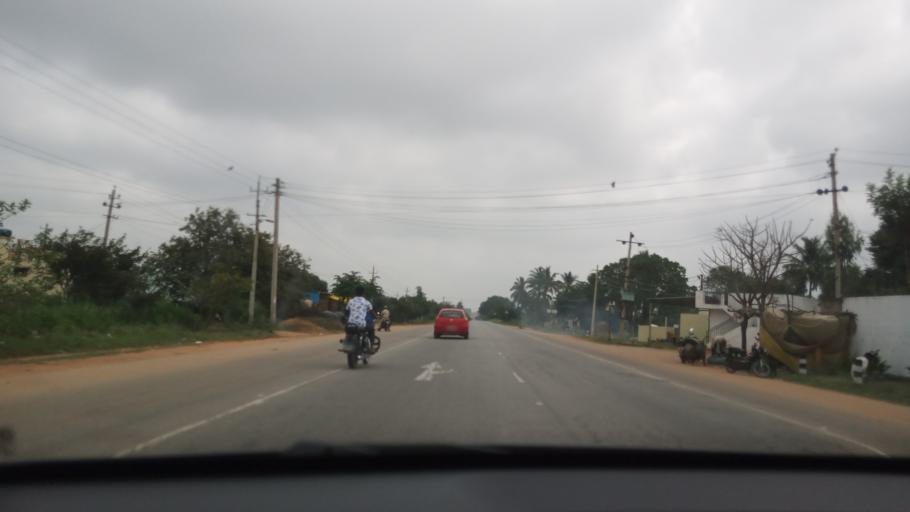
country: IN
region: Karnataka
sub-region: Chikkaballapur
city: Chintamani
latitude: 13.3459
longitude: 78.0180
